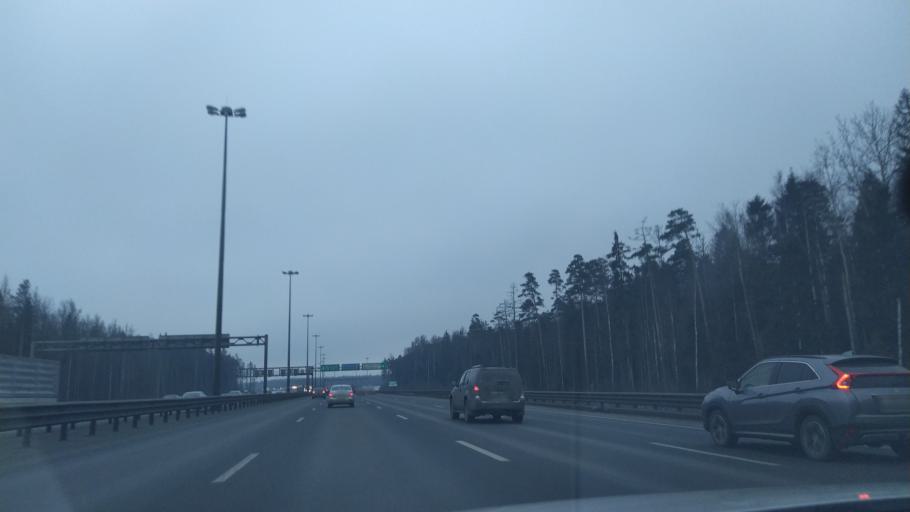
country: RU
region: Leningrad
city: Yanino Vtoroye
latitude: 59.9534
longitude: 30.5475
